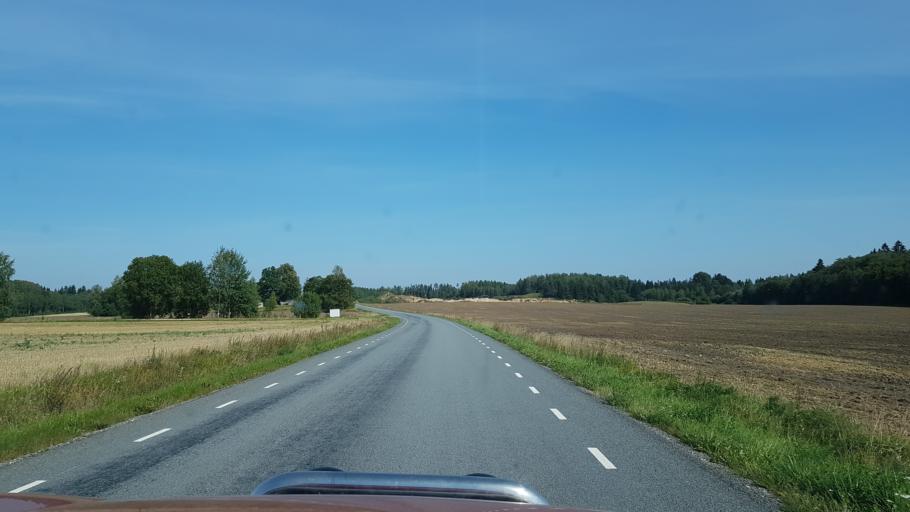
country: EE
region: Viljandimaa
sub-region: Vohma linn
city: Vohma
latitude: 58.5056
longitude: 25.6072
